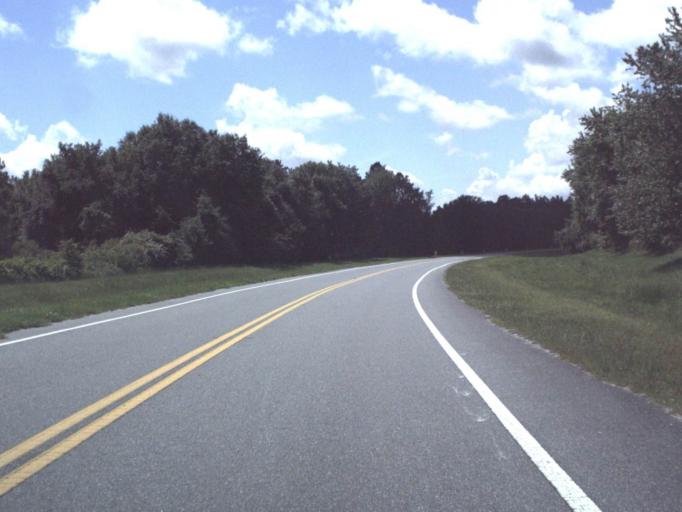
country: US
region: Florida
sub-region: Bradford County
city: Starke
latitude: 30.0194
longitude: -82.0500
